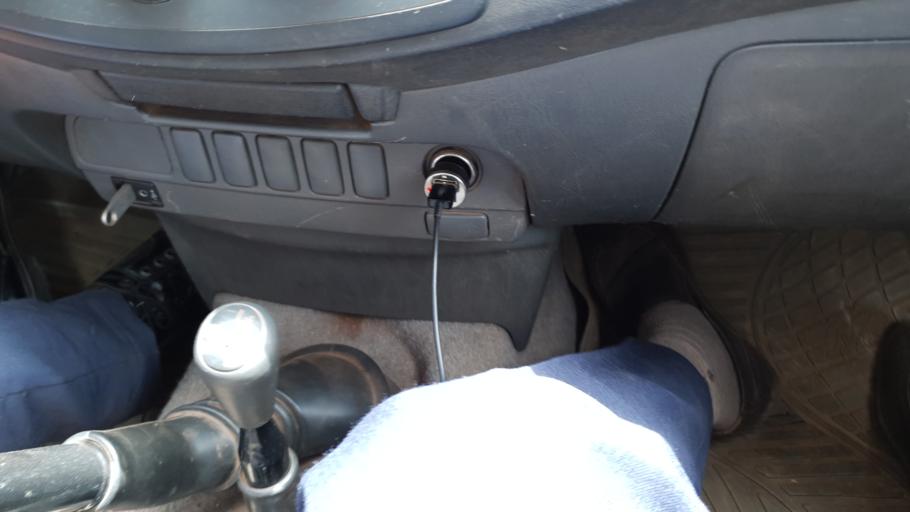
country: ML
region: Koulikoro
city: Kolokani
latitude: 13.3216
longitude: -8.2735
